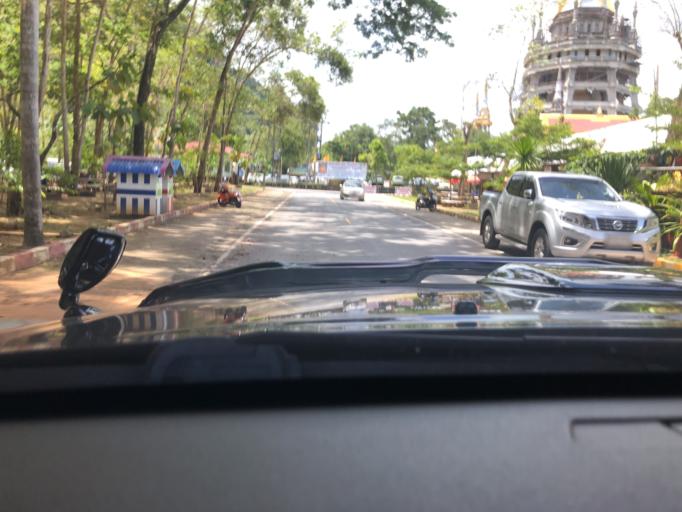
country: TH
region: Krabi
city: Krabi
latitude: 8.1230
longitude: 98.9245
